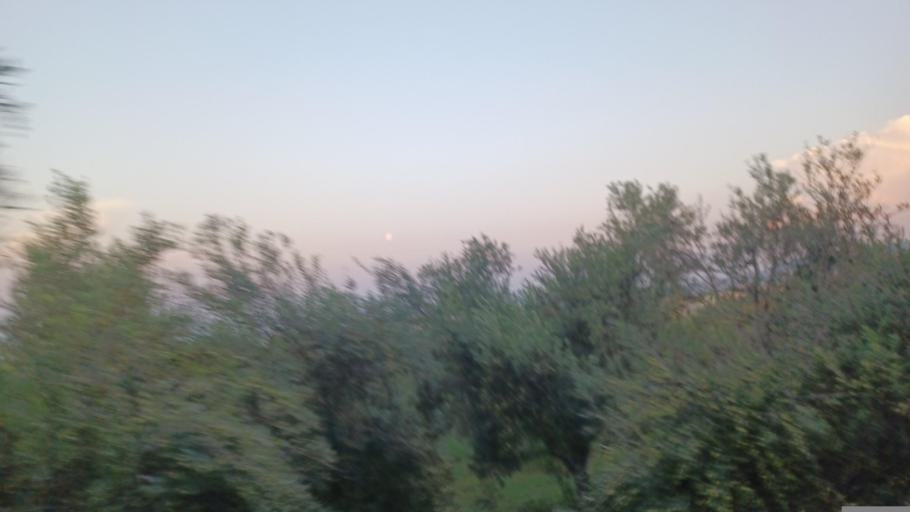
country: CY
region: Pafos
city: Kissonerga
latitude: 34.8431
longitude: 32.4049
